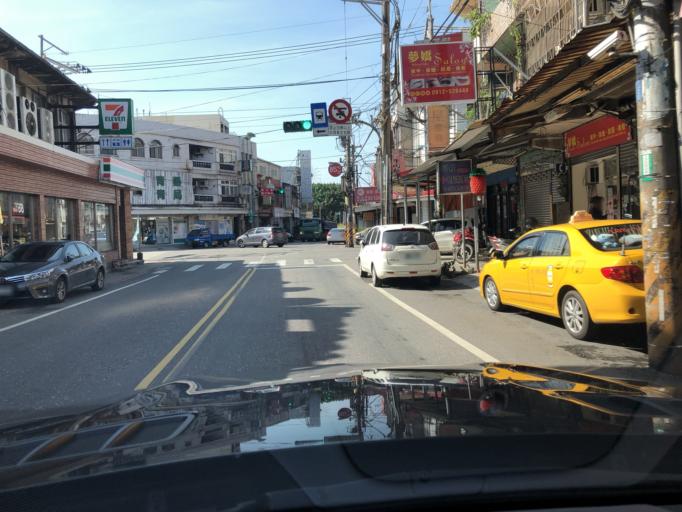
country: TW
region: Taiwan
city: Taoyuan City
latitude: 25.0854
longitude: 121.2868
